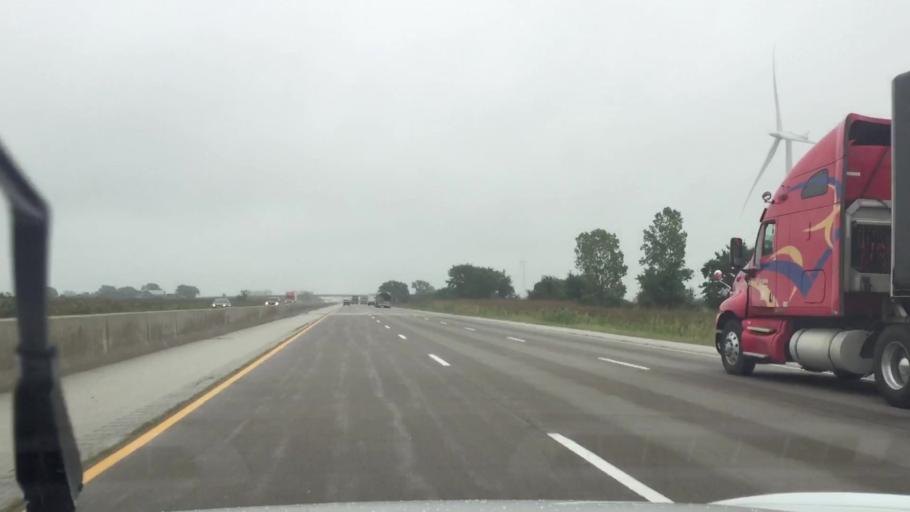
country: US
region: Michigan
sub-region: Wayne County
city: Grosse Pointe Farms
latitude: 42.2356
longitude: -82.6830
